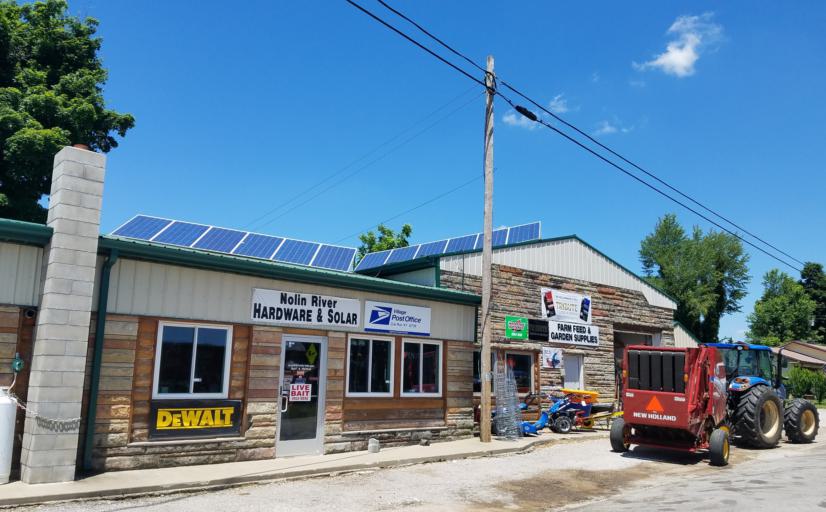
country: US
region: Kentucky
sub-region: Hart County
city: Munfordville
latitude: 37.3047
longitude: -86.0604
